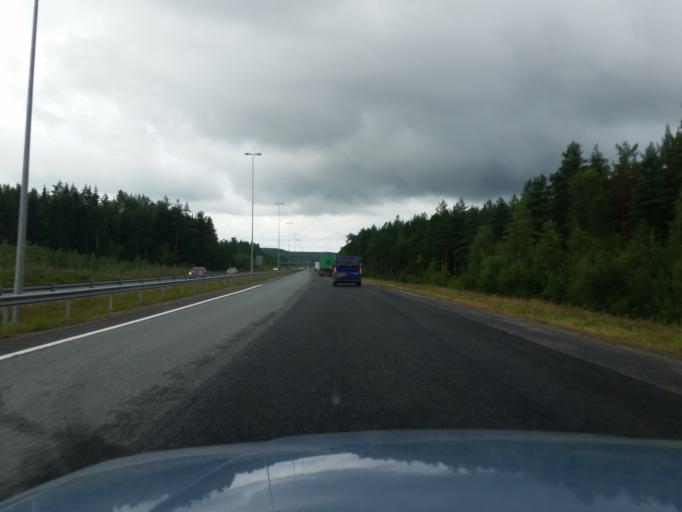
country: FI
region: Uusimaa
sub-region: Helsinki
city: Lohja
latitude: 60.2993
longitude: 24.1884
